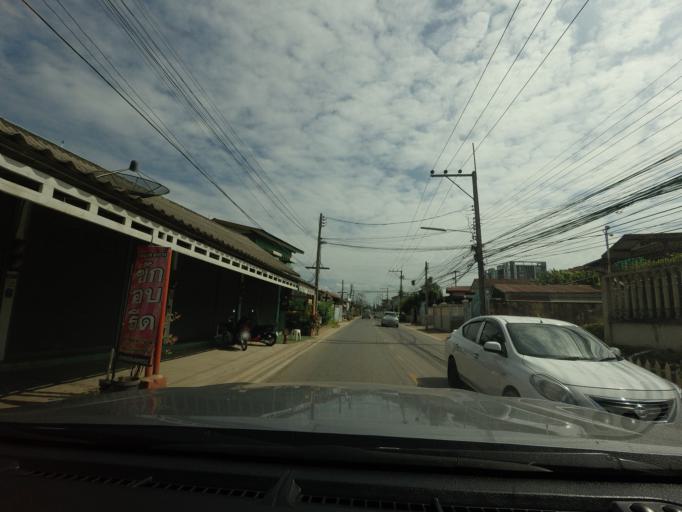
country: TH
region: Phitsanulok
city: Phitsanulok
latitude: 16.7968
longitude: 100.2540
